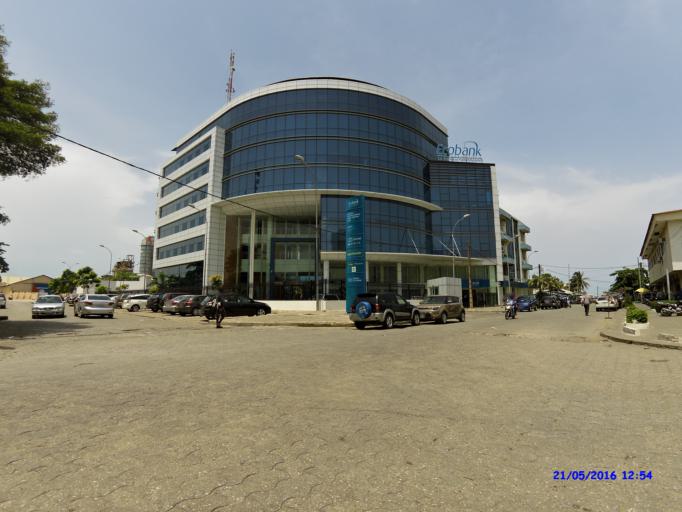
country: BJ
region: Littoral
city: Cotonou
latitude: 6.3530
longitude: 2.4369
